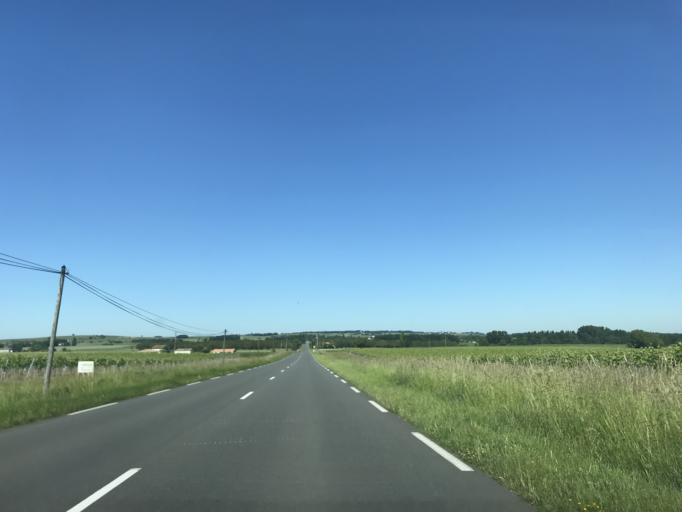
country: FR
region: Poitou-Charentes
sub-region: Departement de la Charente
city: Barbezieux-Saint-Hilaire
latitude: 45.4947
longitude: -0.2160
